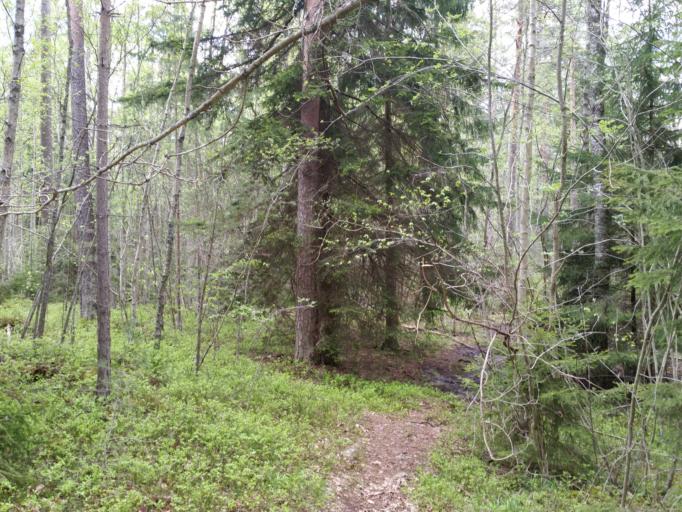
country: SE
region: Stockholm
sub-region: Sollentuna Kommun
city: Sollentuna
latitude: 59.4645
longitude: 17.9535
